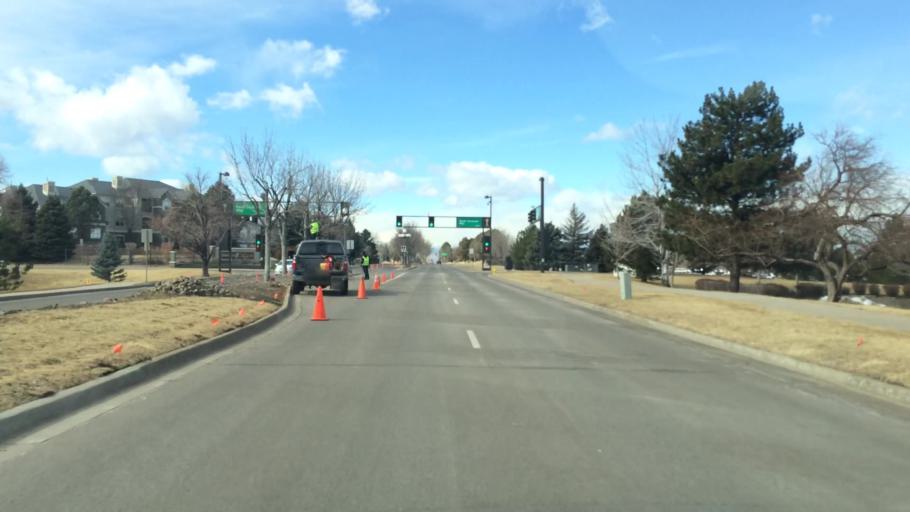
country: US
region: Colorado
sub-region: Arapahoe County
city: Castlewood
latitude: 39.6023
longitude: -104.8984
